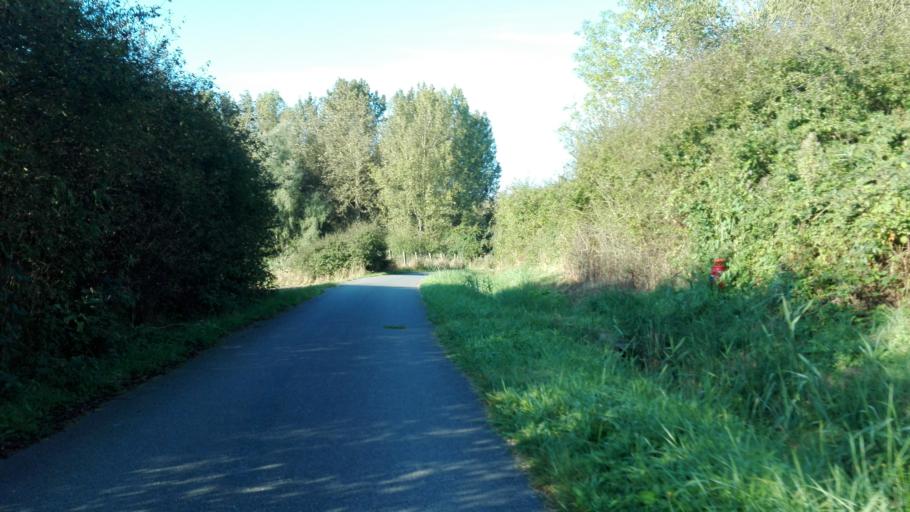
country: FR
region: Nord-Pas-de-Calais
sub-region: Departement du Nord
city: Watten
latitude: 50.8281
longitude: 2.1933
